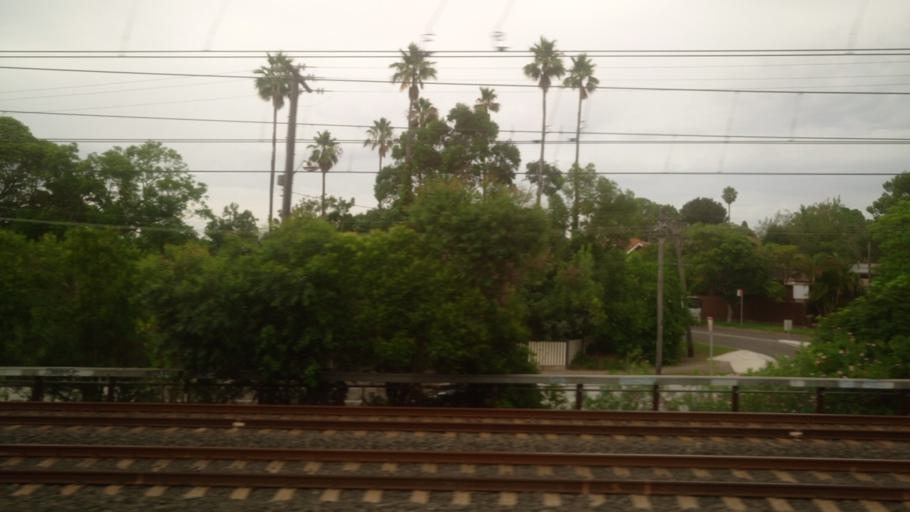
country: AU
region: New South Wales
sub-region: Ashfield
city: Croydon
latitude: -33.8802
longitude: 151.1115
